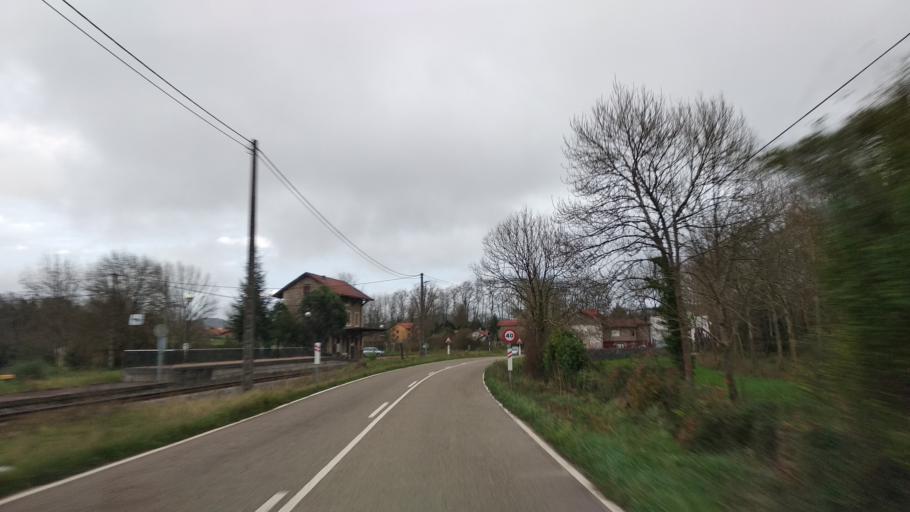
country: ES
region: Cantabria
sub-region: Provincia de Cantabria
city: Entrambasaguas
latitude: 43.4107
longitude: -3.7044
